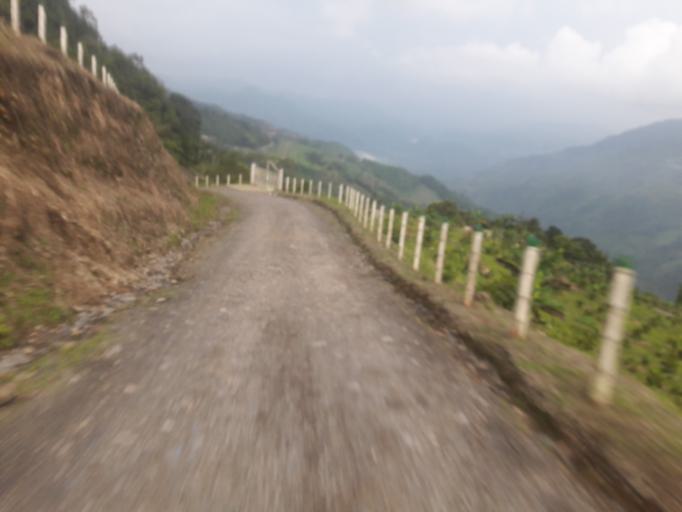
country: CO
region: Boyaca
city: Quipama
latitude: 5.5349
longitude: -74.1888
